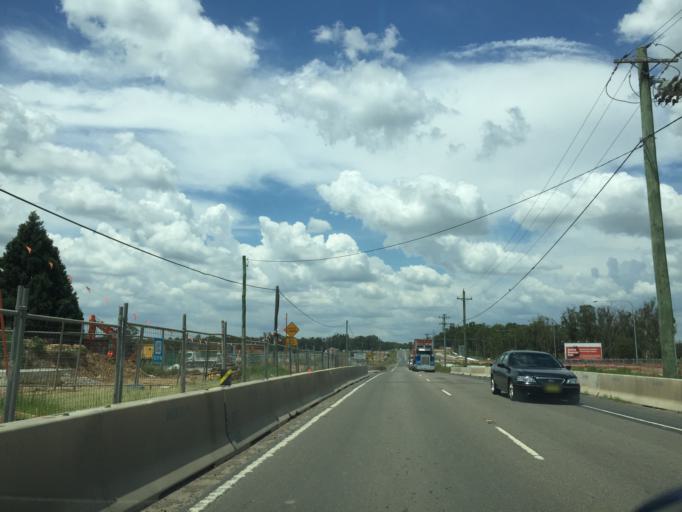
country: AU
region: New South Wales
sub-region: Blacktown
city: Hassall Grove
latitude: -33.7071
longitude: 150.8393
